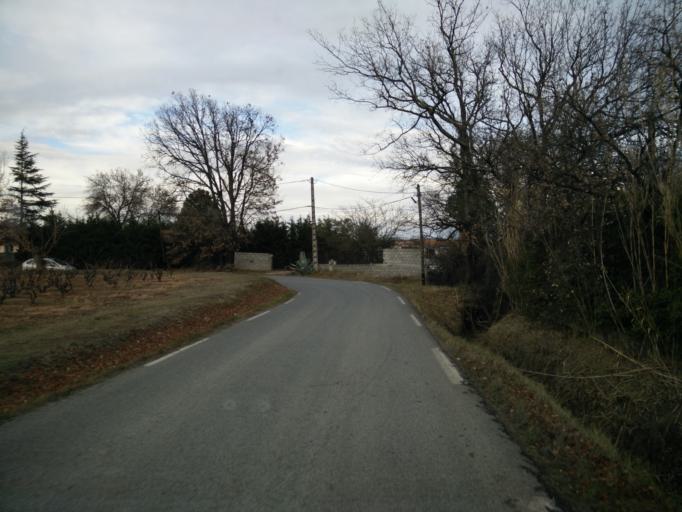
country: FR
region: Provence-Alpes-Cote d'Azur
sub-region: Departement du Var
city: Vidauban
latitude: 43.4088
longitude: 6.4362
